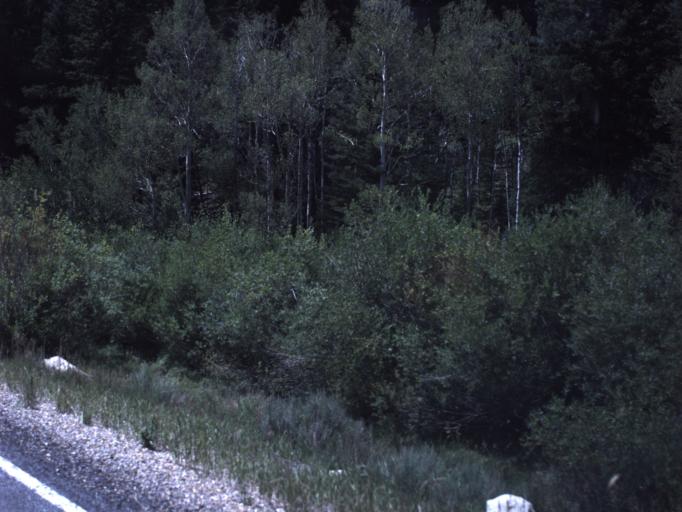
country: US
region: Utah
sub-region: Sanpete County
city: Fairview
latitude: 39.6717
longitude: -111.1555
